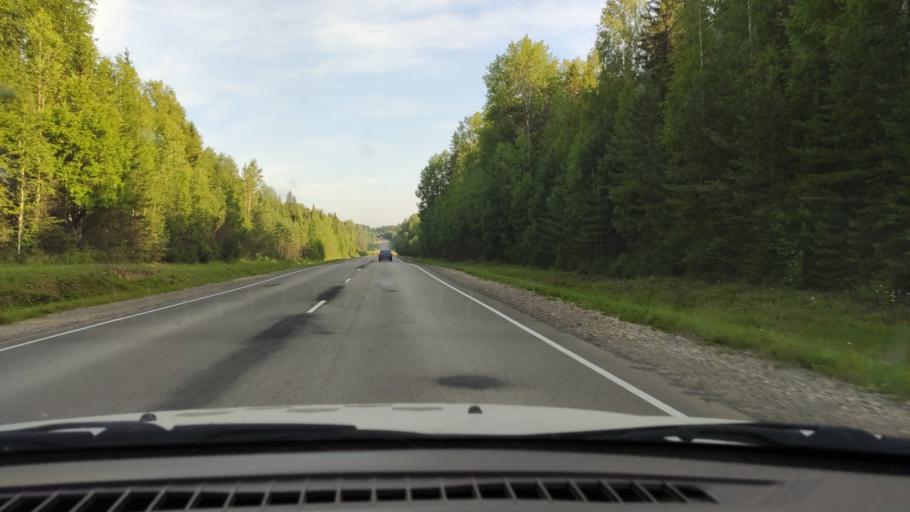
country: RU
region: Kirov
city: Chernaya Kholunitsa
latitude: 58.8425
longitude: 51.7489
